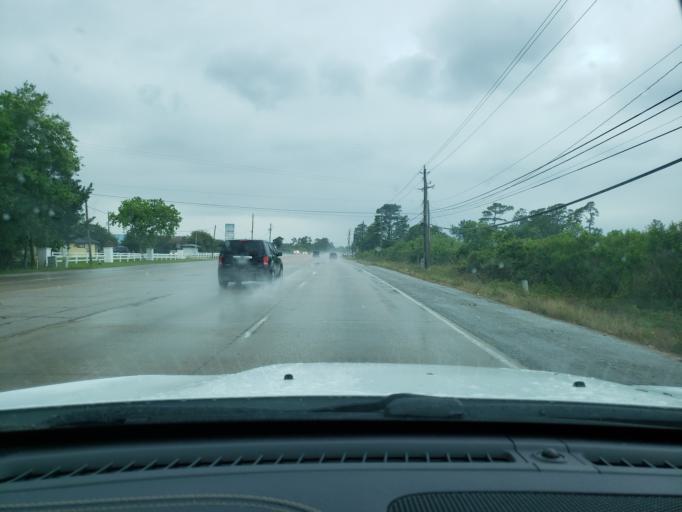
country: US
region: Texas
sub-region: Chambers County
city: Mont Belvieu
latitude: 29.7894
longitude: -94.9109
